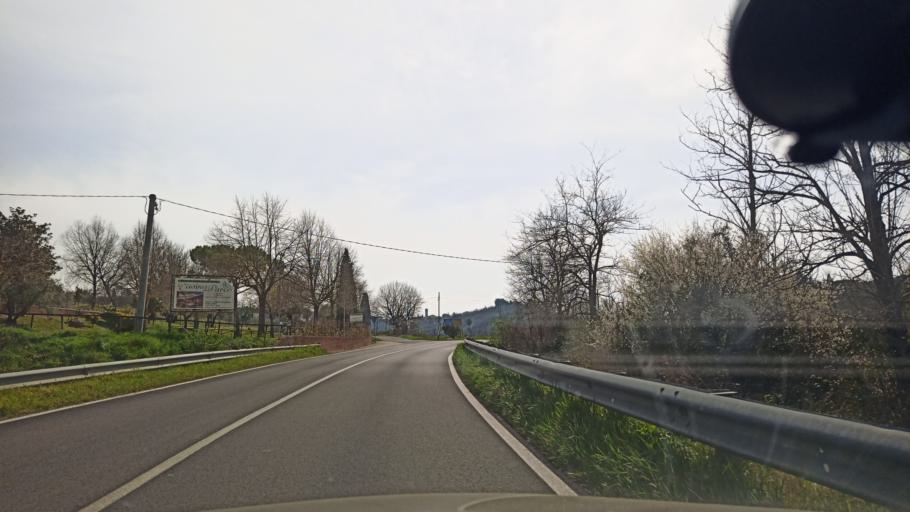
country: IT
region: Latium
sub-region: Provincia di Rieti
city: Cantalupo in Sabina
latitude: 42.3195
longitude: 12.6450
